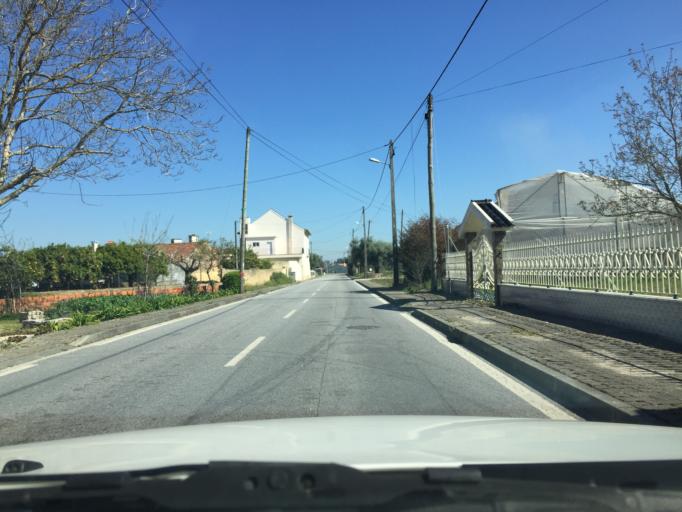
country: PT
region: Aveiro
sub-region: Anadia
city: Sangalhos
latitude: 40.4290
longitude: -8.5132
